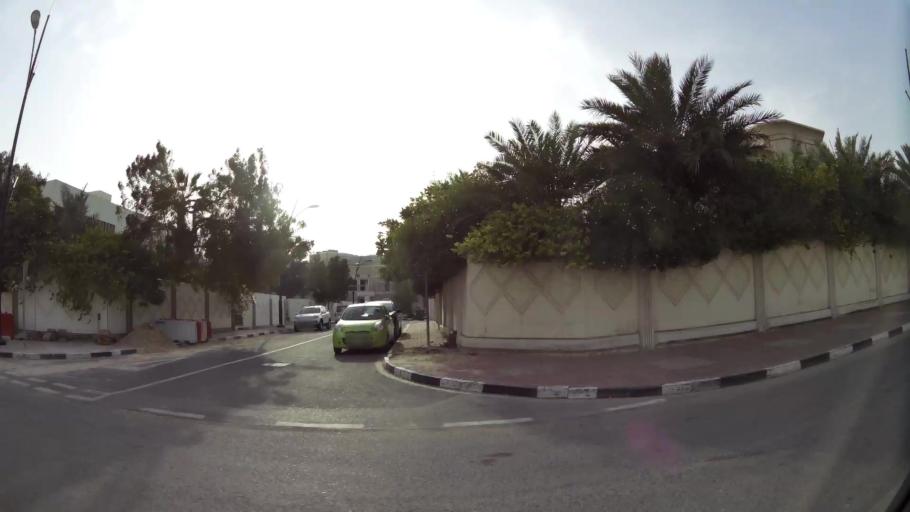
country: QA
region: Baladiyat ad Dawhah
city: Doha
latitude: 25.3303
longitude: 51.5199
